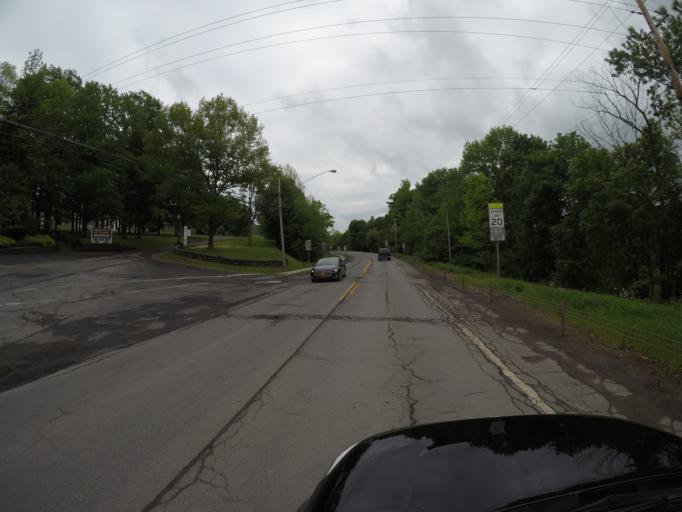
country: US
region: New York
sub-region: Delaware County
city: Delhi
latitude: 42.2738
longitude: -74.9162
